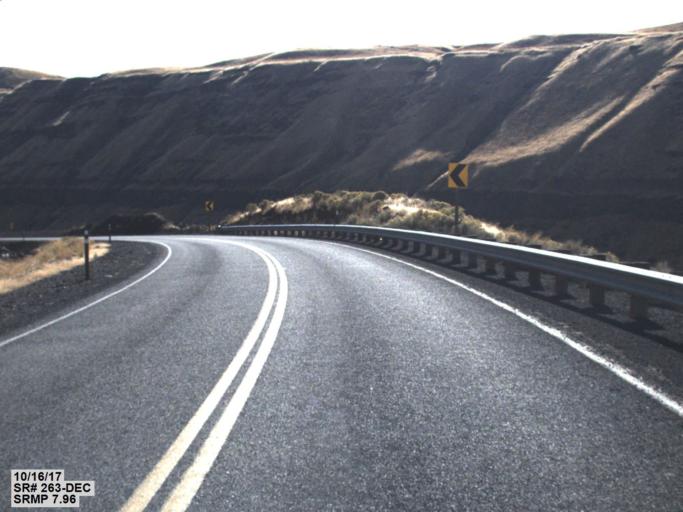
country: US
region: Washington
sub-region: Franklin County
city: Connell
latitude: 46.6283
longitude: -118.5609
